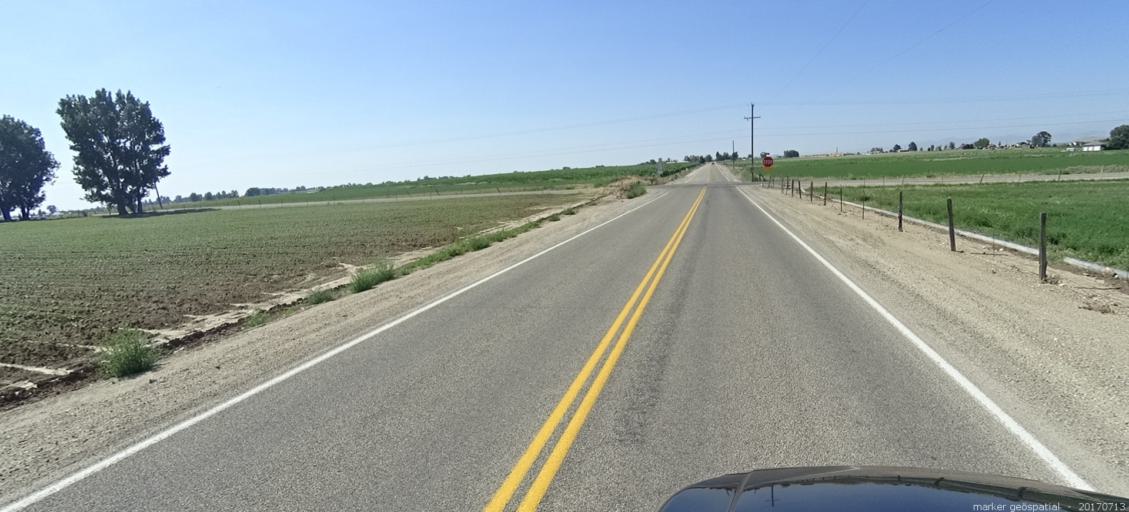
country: US
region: Idaho
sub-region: Ada County
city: Kuna
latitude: 43.5036
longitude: -116.3743
